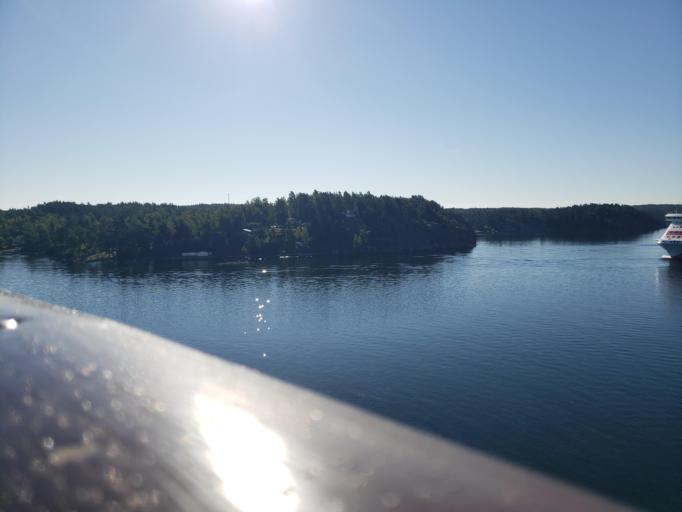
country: SE
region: Stockholm
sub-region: Varmdo Kommun
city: Mortnas
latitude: 59.3859
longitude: 18.4432
